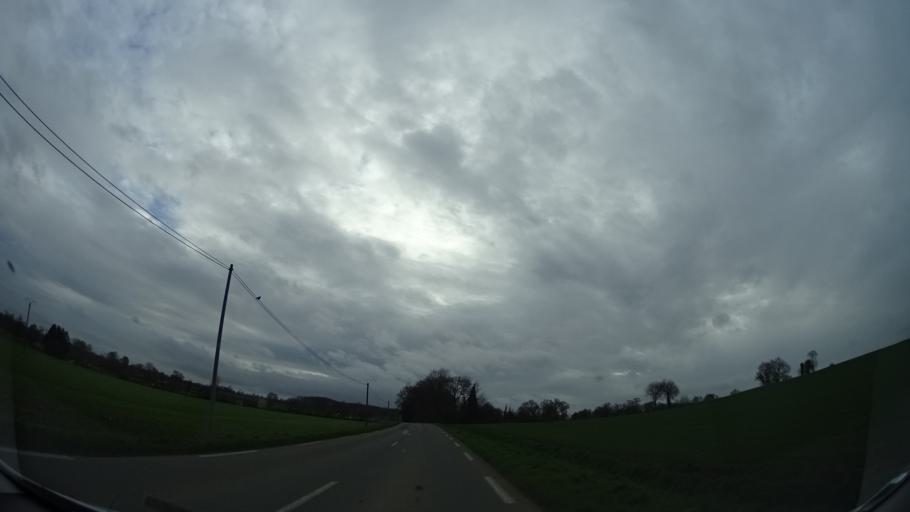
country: FR
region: Brittany
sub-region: Departement des Cotes-d'Armor
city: Evran
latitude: 48.3669
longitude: -1.9705
